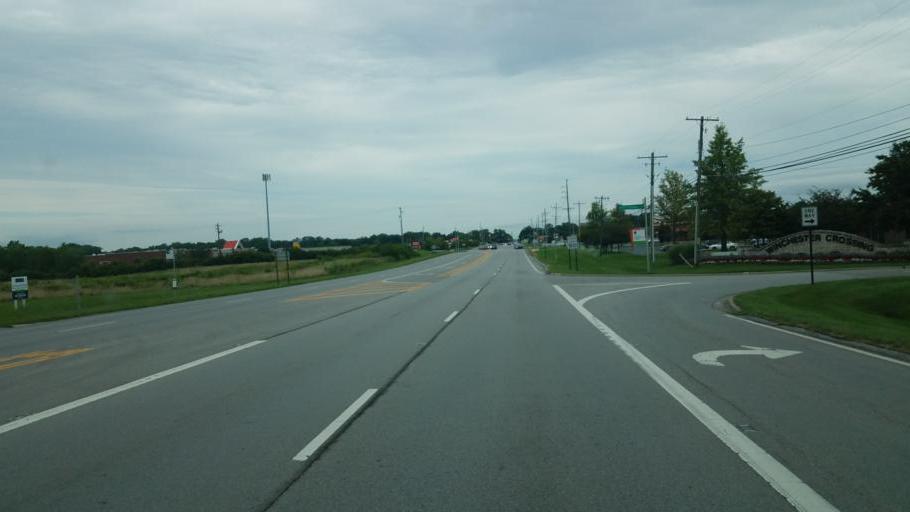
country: US
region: Ohio
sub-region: Franklin County
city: Groveport
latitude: 39.8927
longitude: -82.8826
